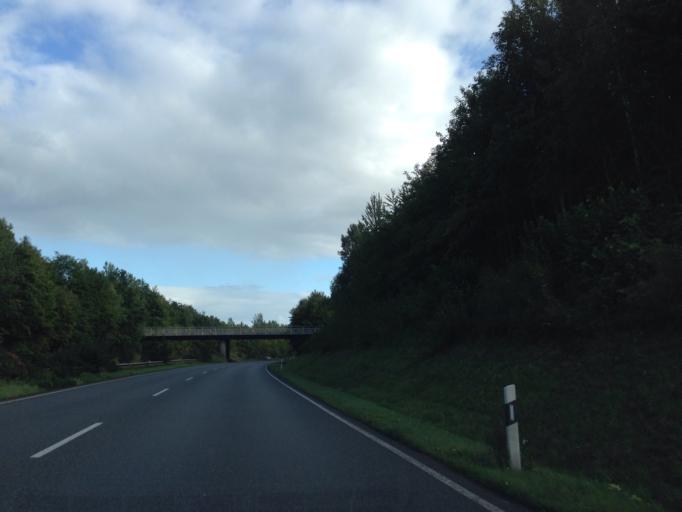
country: DE
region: Lower Saxony
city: Wendisch Evern
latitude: 53.2470
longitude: 10.4509
